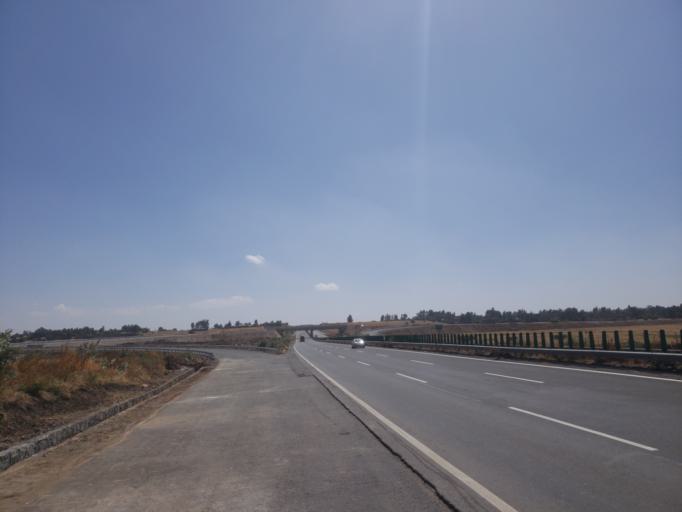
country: ET
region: Oromiya
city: Mojo
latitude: 8.5821
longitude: 39.1700
